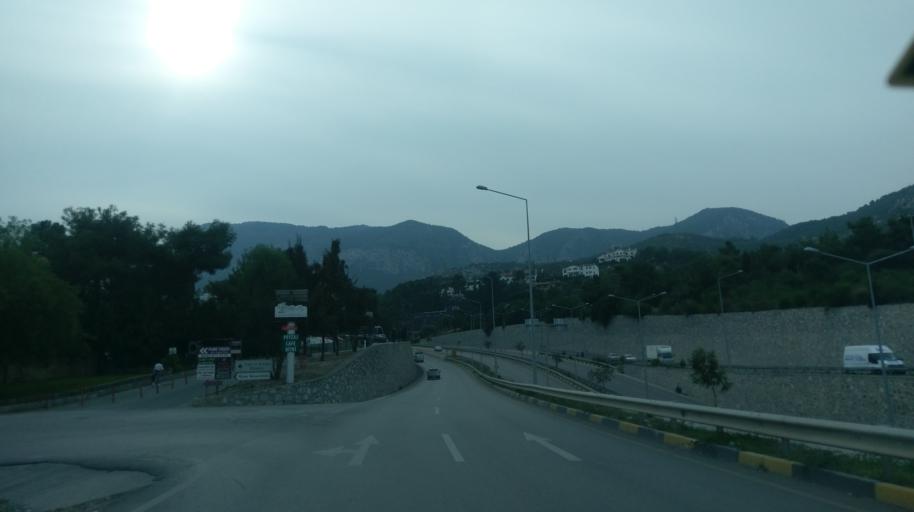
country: CY
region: Keryneia
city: Kyrenia
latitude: 35.3248
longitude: 33.3181
